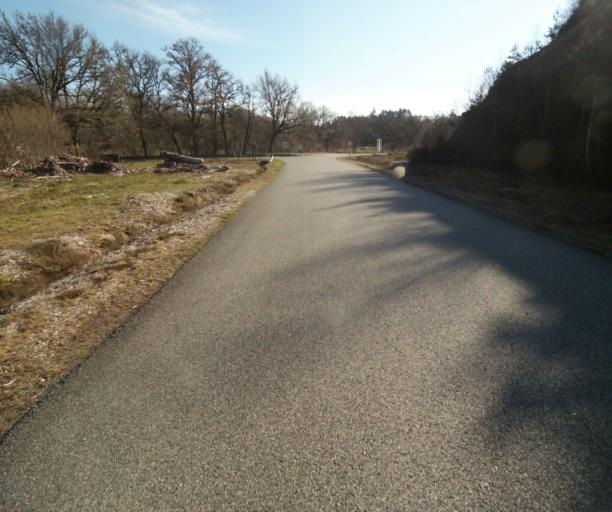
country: FR
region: Limousin
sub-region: Departement de la Correze
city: Correze
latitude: 45.3118
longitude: 1.8864
